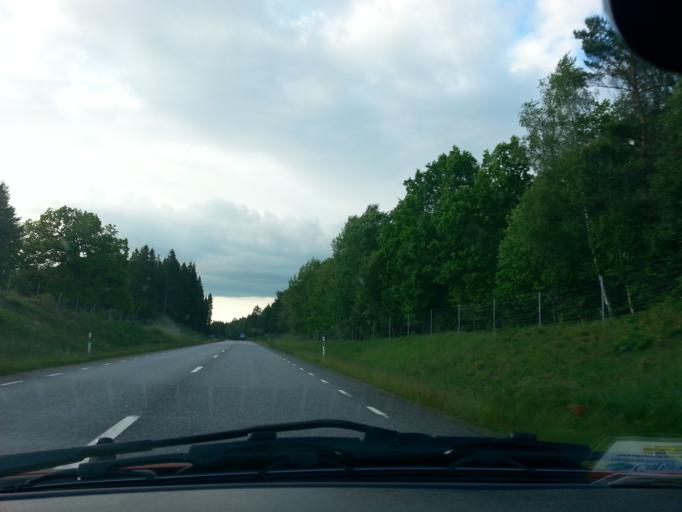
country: SE
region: Vaestra Goetaland
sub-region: Tranemo Kommun
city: Limmared
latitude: 57.5280
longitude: 13.3411
